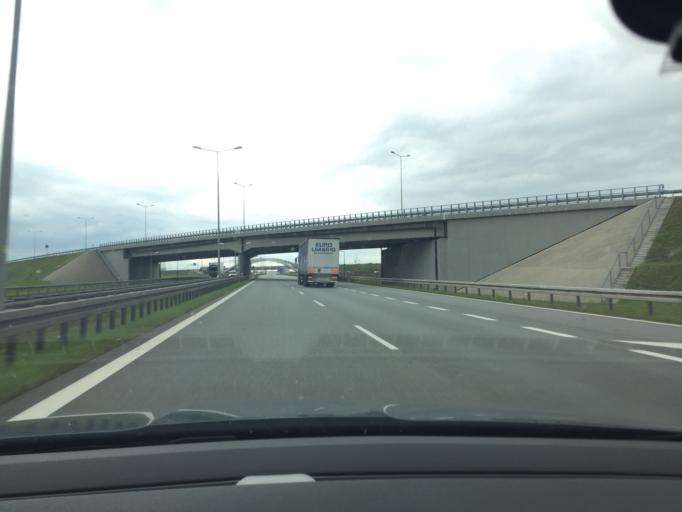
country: PL
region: Greater Poland Voivodeship
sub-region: Powiat poznanski
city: Komorniki
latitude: 52.3507
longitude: 16.7701
